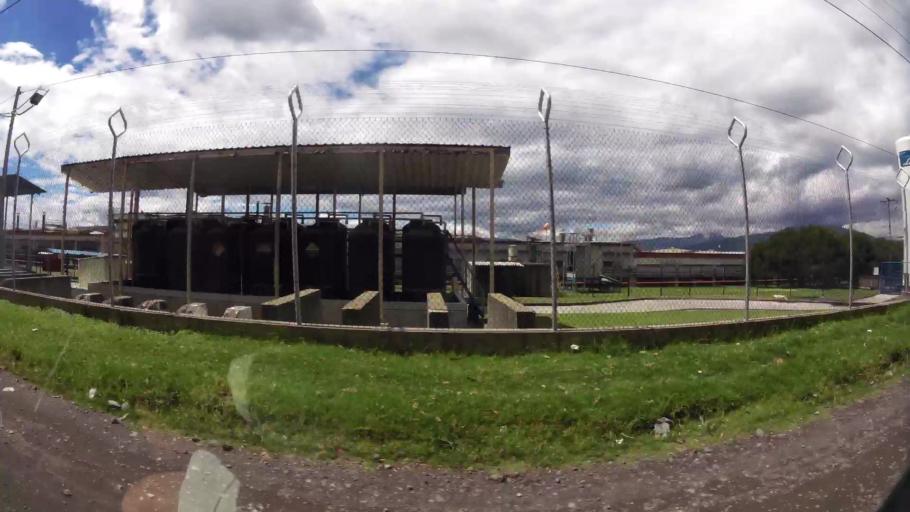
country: EC
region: Pichincha
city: Sangolqui
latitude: -0.3452
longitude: -78.5447
